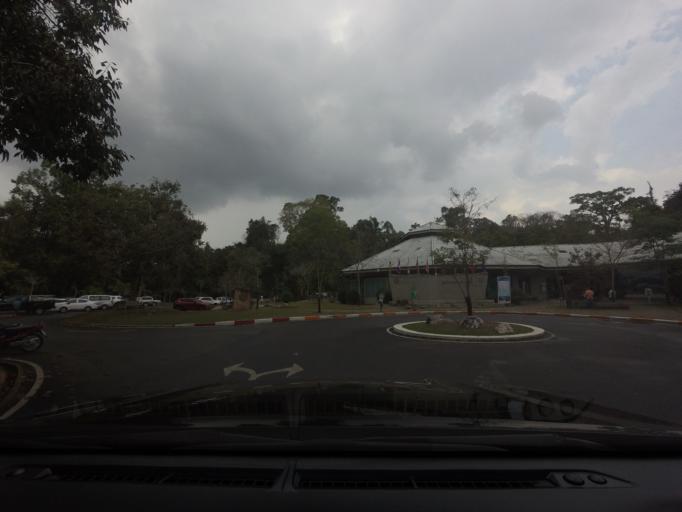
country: TH
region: Nakhon Ratchasima
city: Pak Chong
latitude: 14.4376
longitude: 101.3712
